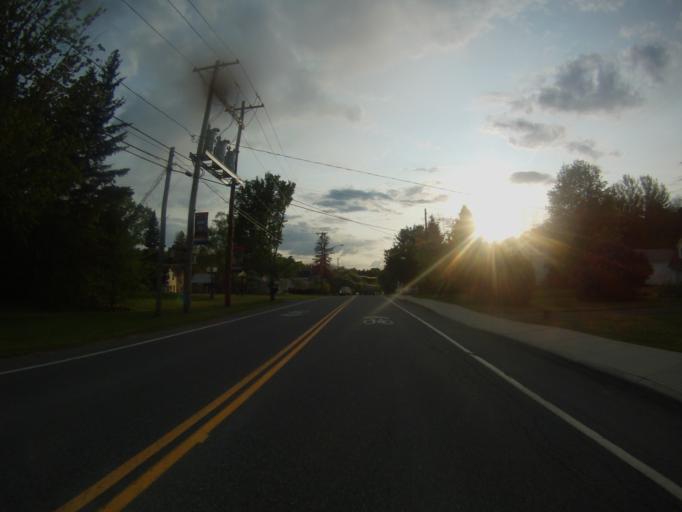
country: US
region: New York
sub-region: Essex County
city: Ticonderoga
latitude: 43.9506
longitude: -73.4227
